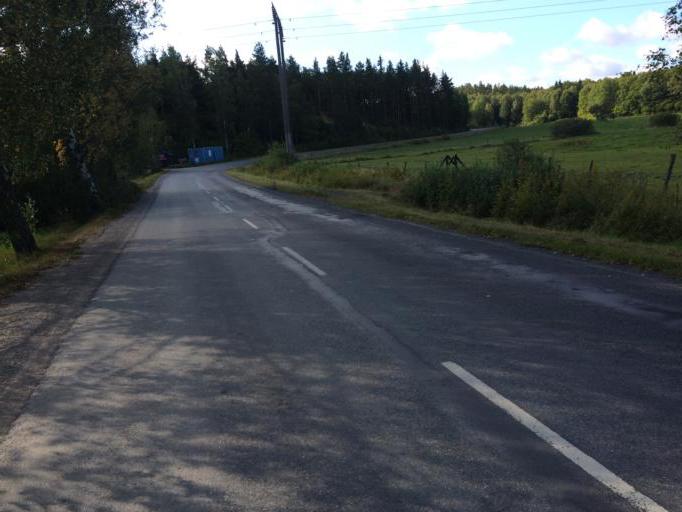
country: SE
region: Stockholm
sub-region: Haninge Kommun
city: Handen
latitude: 59.2179
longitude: 18.0820
